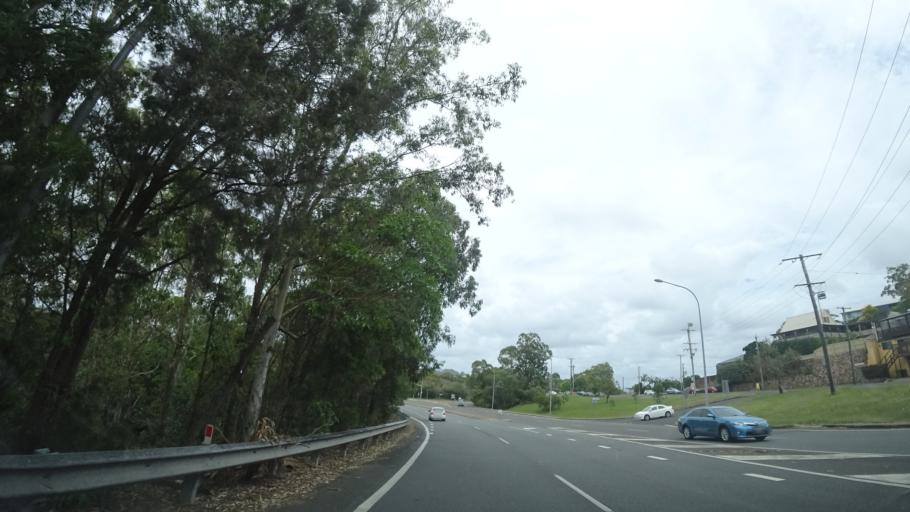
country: AU
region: Queensland
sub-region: Sunshine Coast
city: Mooloolaba
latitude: -26.6743
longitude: 153.0991
